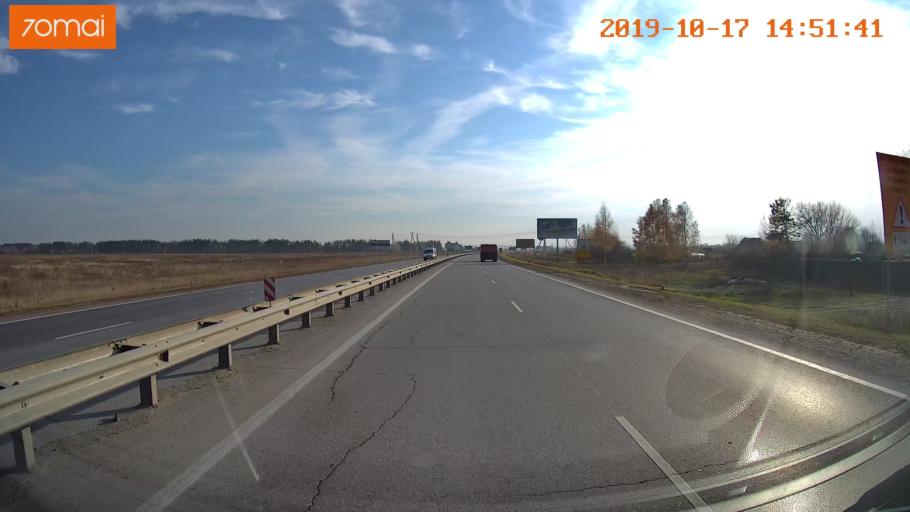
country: RU
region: Rjazan
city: Polyany
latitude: 54.7155
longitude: 39.8483
